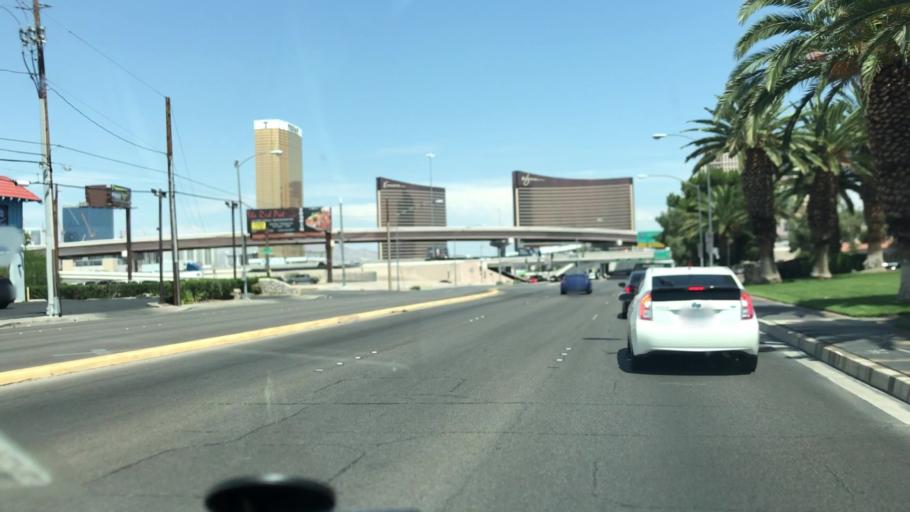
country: US
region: Nevada
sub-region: Clark County
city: Paradise
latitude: 36.1263
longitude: -115.1840
